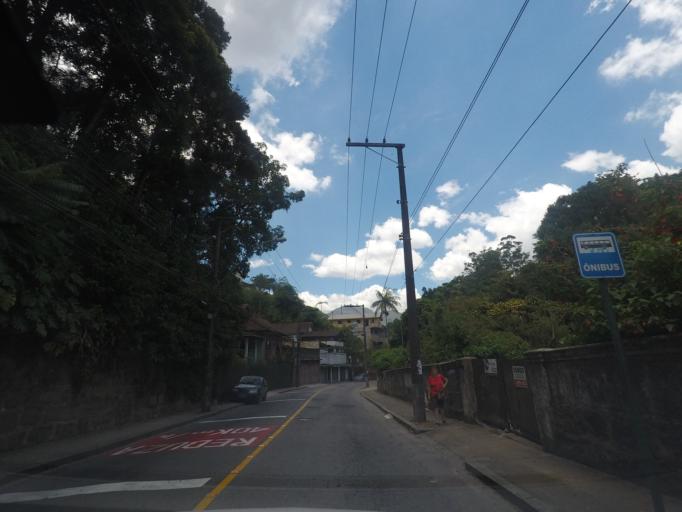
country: BR
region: Rio de Janeiro
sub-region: Petropolis
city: Petropolis
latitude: -22.5006
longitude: -43.1687
